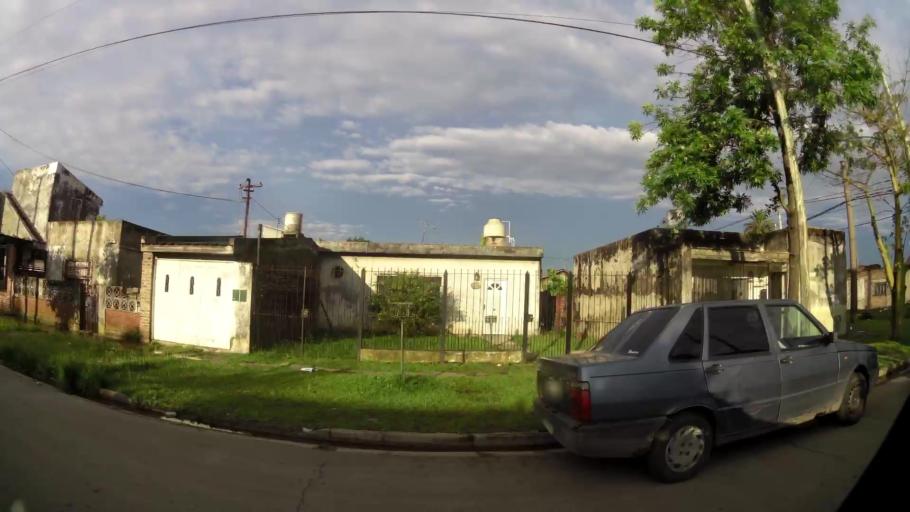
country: AR
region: Buenos Aires
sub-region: Partido de Lomas de Zamora
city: Lomas de Zamora
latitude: -34.7555
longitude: -58.3534
